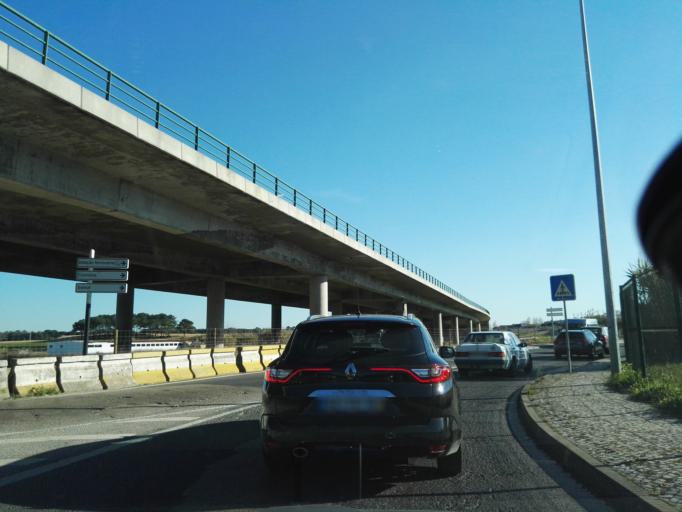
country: PT
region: Setubal
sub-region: Seixal
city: Corroios
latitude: 38.6417
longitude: -9.1490
